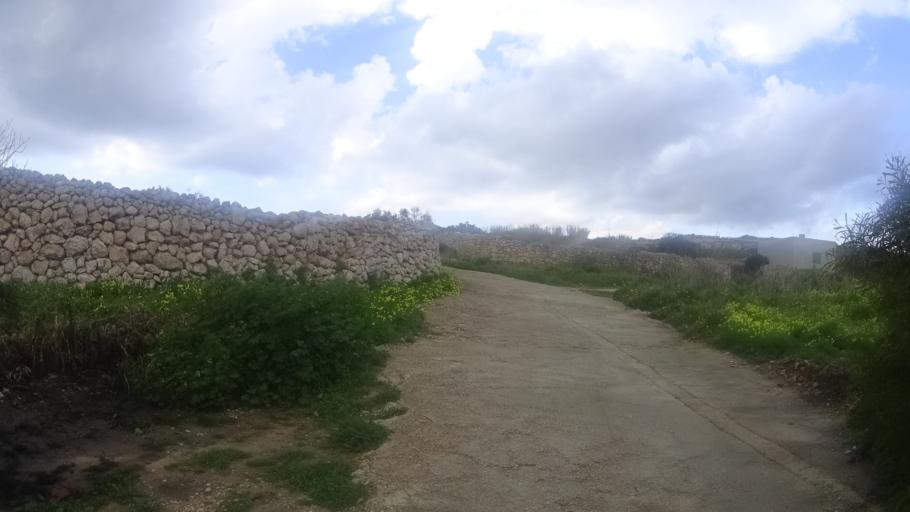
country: MT
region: L-Imtarfa
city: Imtarfa
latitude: 35.8951
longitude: 14.3731
